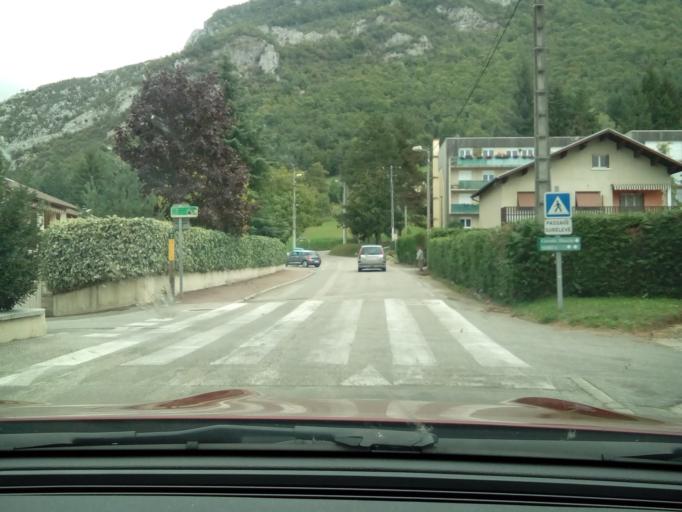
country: FR
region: Rhone-Alpes
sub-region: Departement de l'Isere
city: Pont-en-Royans
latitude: 45.0463
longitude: 5.3439
